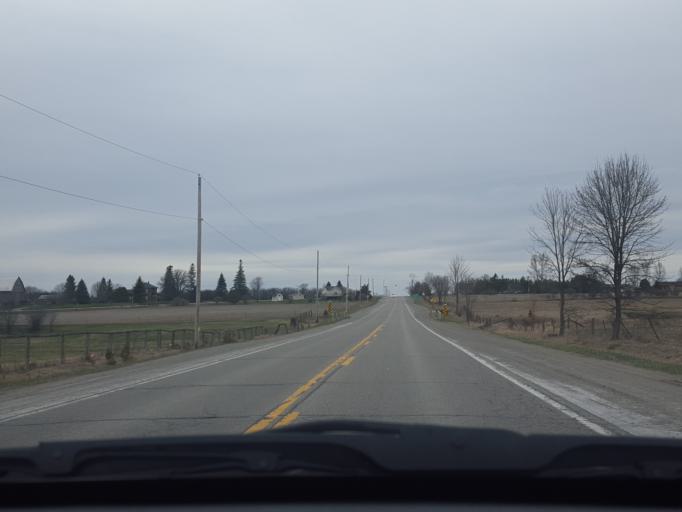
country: CA
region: Ontario
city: Uxbridge
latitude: 44.3147
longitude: -79.1788
